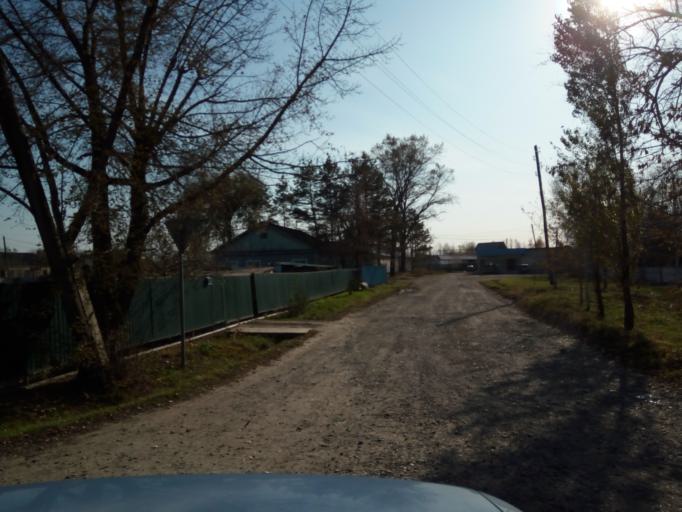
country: RU
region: Primorskiy
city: Dal'nerechensk
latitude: 45.9221
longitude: 133.7493
